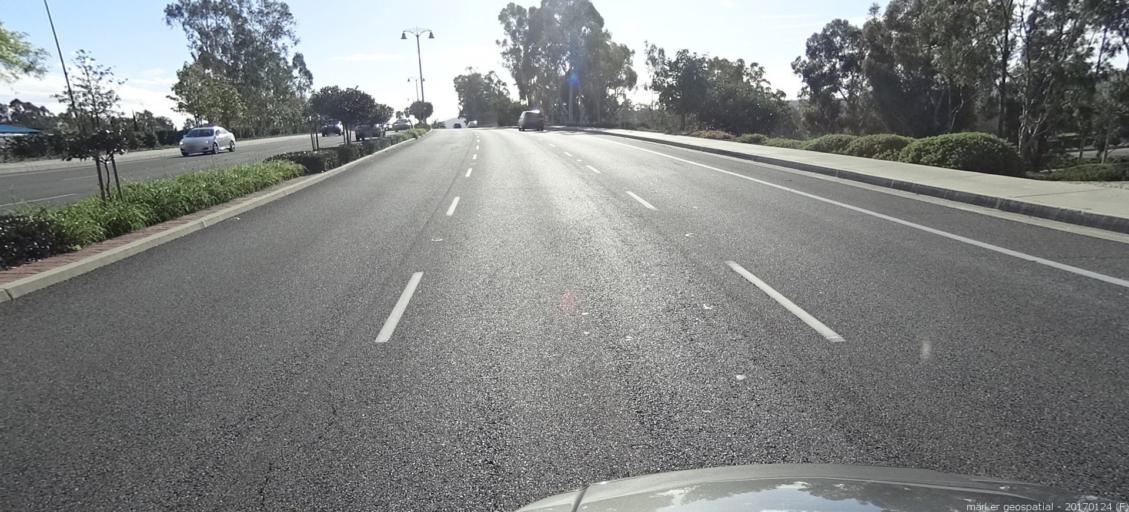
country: US
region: California
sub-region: Orange County
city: Lake Forest
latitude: 33.6221
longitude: -117.6862
